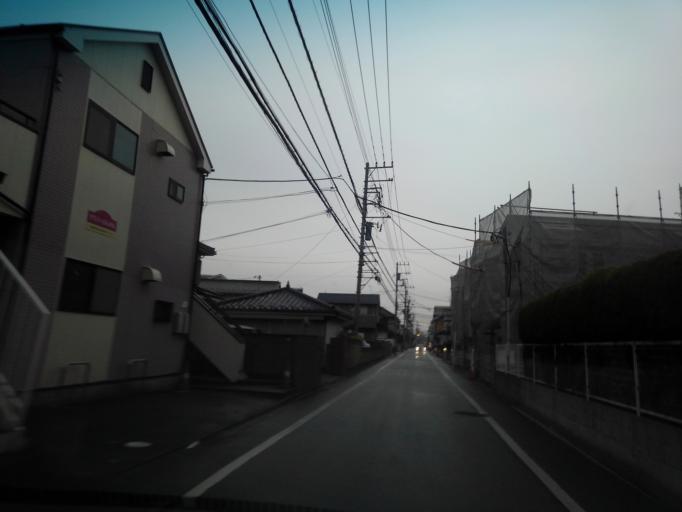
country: JP
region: Tokyo
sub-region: Machida-shi
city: Machida
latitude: 35.5128
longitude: 139.4423
